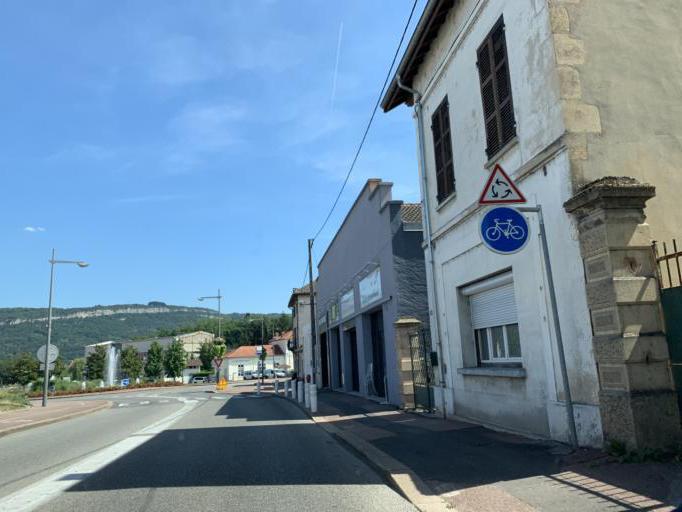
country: FR
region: Rhone-Alpes
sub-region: Departement de l'Ain
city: Belley
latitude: 45.7589
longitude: 5.6962
